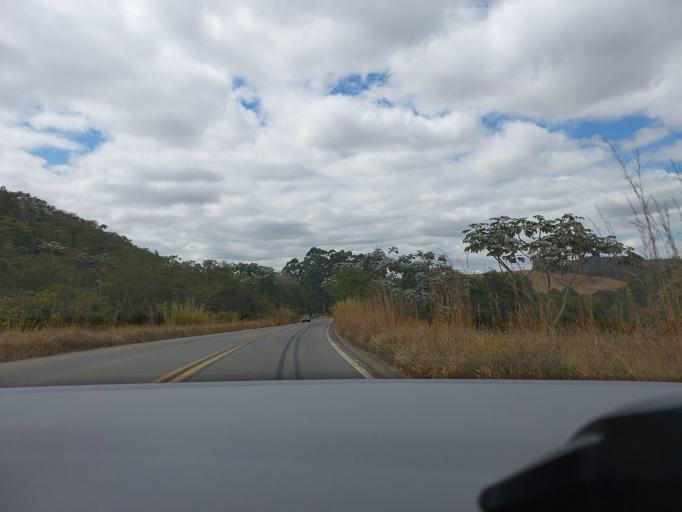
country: BR
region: Minas Gerais
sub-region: Vicosa
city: Vicosa
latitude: -20.8403
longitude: -42.7081
